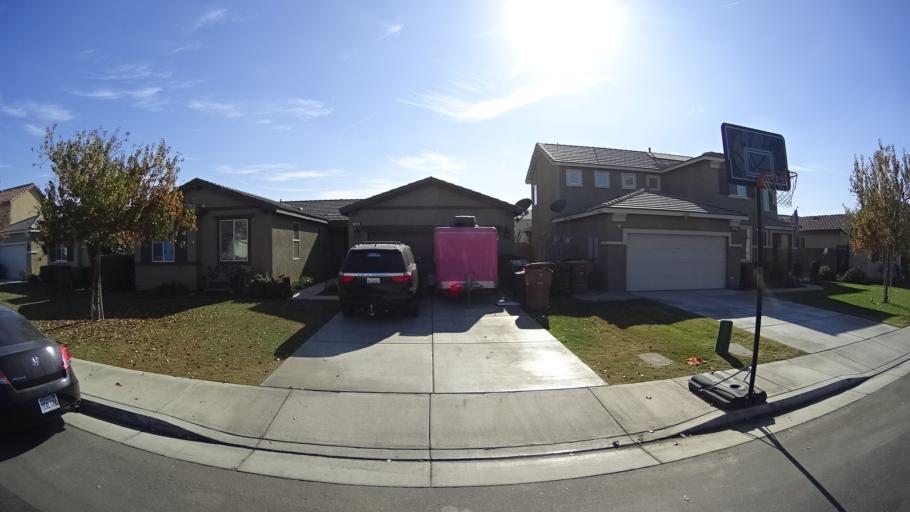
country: US
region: California
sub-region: Kern County
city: Greenfield
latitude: 35.2942
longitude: -119.0633
